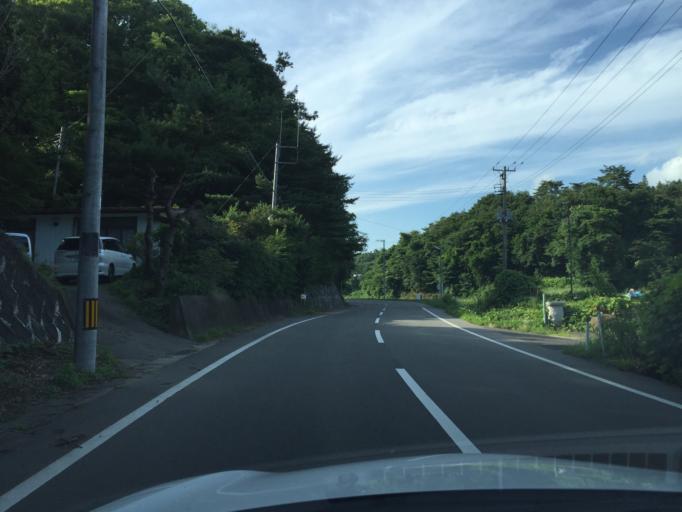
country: JP
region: Fukushima
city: Miharu
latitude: 37.3625
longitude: 140.5185
